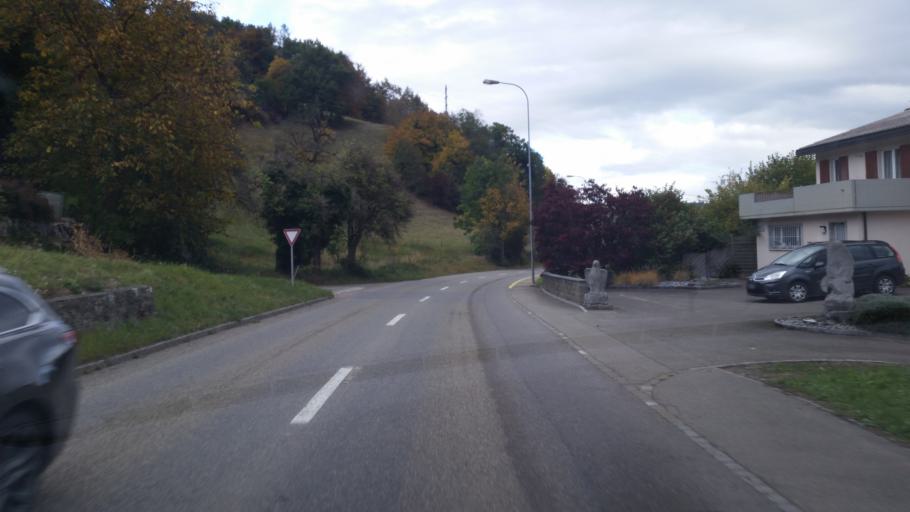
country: CH
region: Aargau
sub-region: Bezirk Brugg
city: Villigen
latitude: 47.5580
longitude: 8.2231
